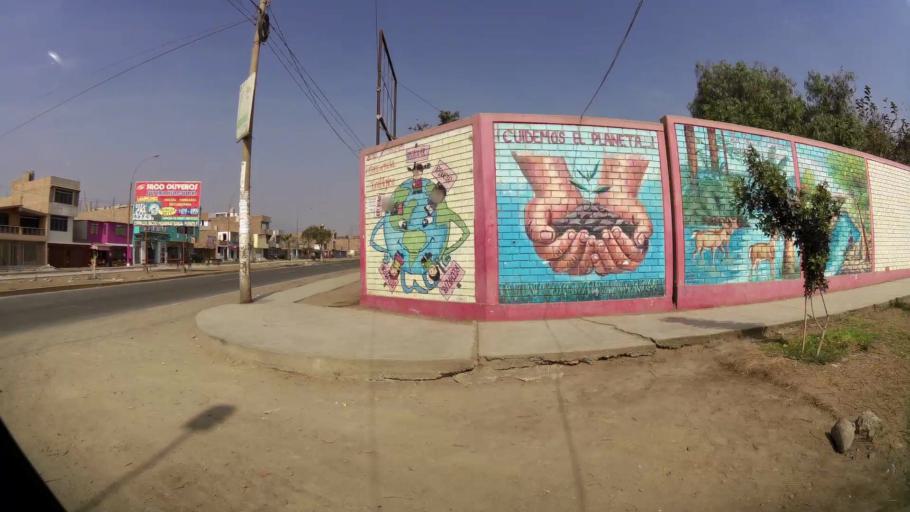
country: PE
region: Lima
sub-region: Lima
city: Santa Rosa
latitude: -11.7827
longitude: -77.1598
